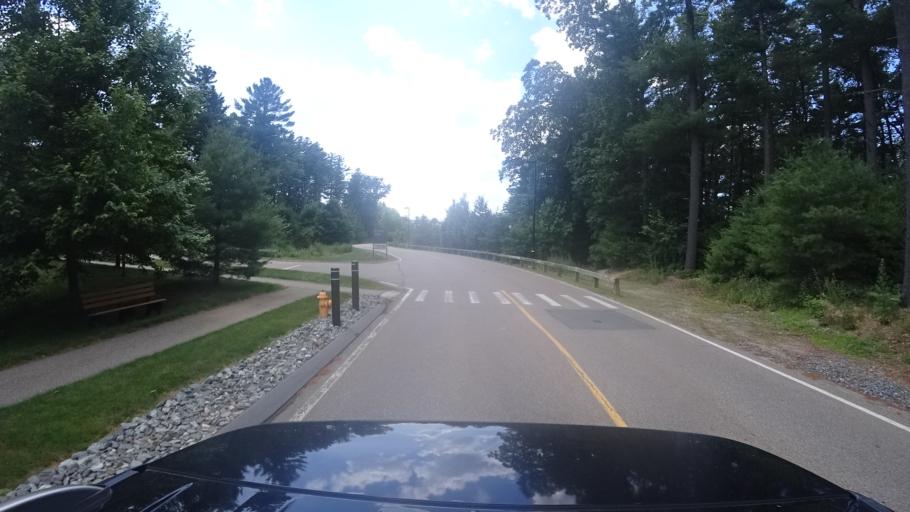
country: US
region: Massachusetts
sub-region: Norfolk County
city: Needham
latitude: 42.2667
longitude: -71.1997
